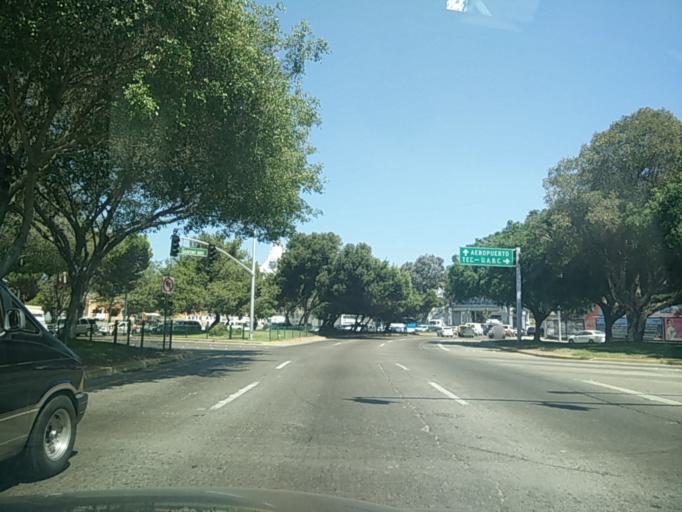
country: MX
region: Baja California
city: Tijuana
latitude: 32.5298
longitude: -117.0130
